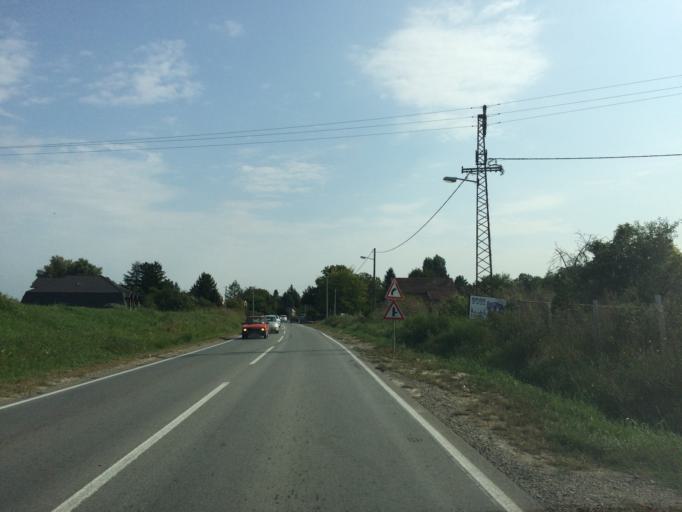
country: RS
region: Autonomna Pokrajina Vojvodina
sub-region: Juznobacki Okrug
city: Novi Sad
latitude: 45.2194
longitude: 19.8242
